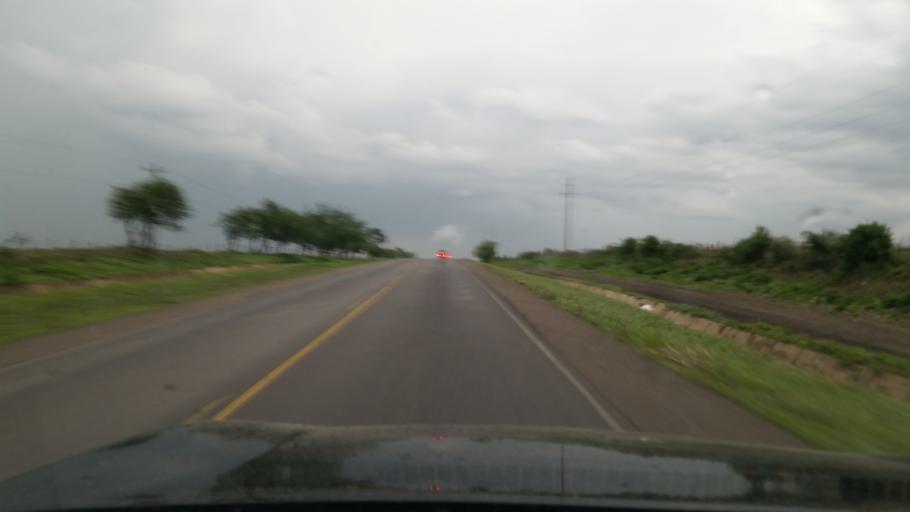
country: NI
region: Chinandega
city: Puerto Morazan
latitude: 12.7906
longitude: -87.0181
